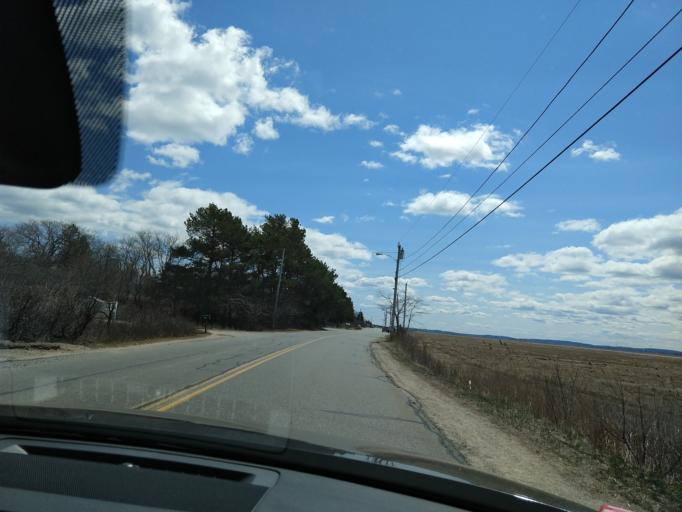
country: US
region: Massachusetts
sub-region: Essex County
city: Salisbury
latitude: 42.7966
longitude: -70.8121
